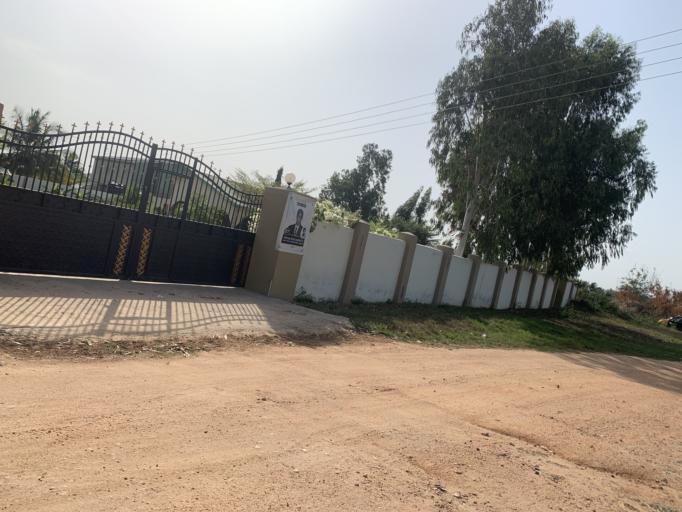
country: GH
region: Central
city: Winneba
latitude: 5.3658
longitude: -0.6465
